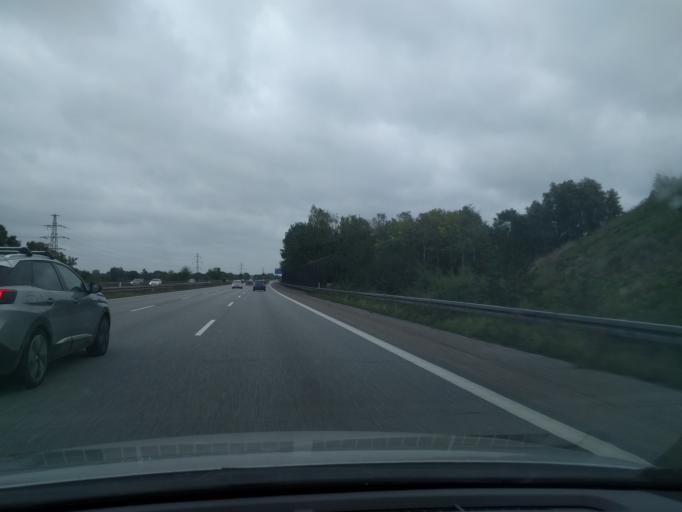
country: DK
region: Capital Region
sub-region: Vallensbaek Kommune
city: Vallensbaek
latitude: 55.6226
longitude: 12.3634
